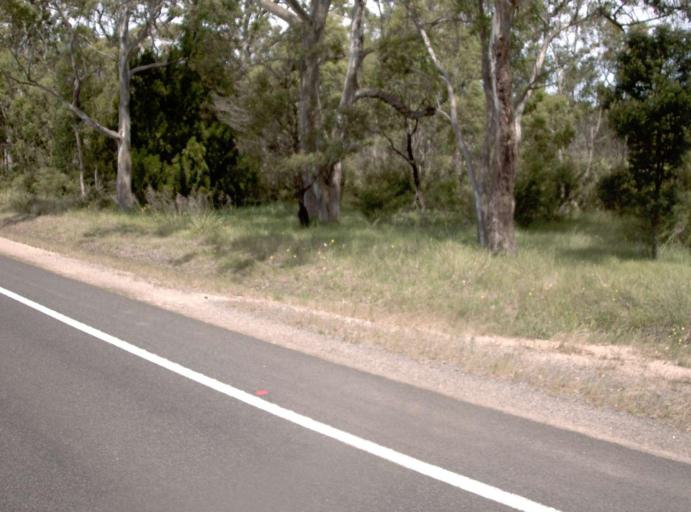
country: AU
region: Victoria
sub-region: Wellington
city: Sale
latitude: -37.9232
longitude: 147.2394
